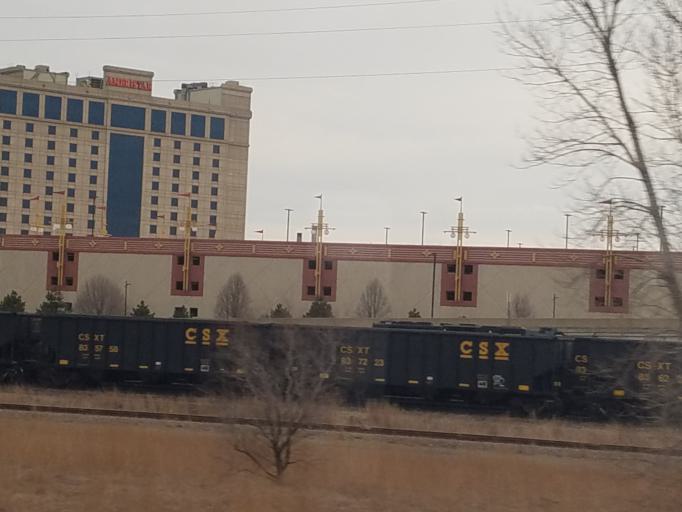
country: US
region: Indiana
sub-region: Lake County
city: East Chicago
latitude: 41.6487
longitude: -87.4369
